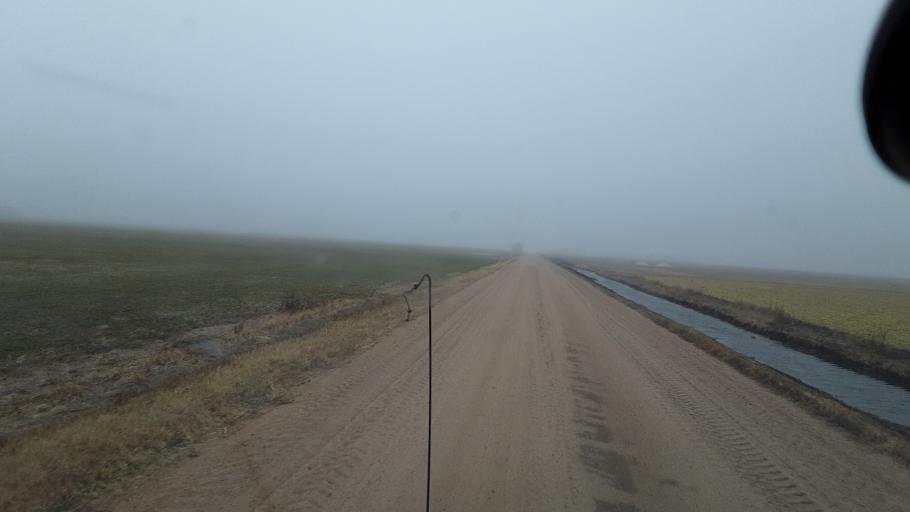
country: US
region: Kansas
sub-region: Reno County
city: South Hutchinson
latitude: 37.9818
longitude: -97.9957
